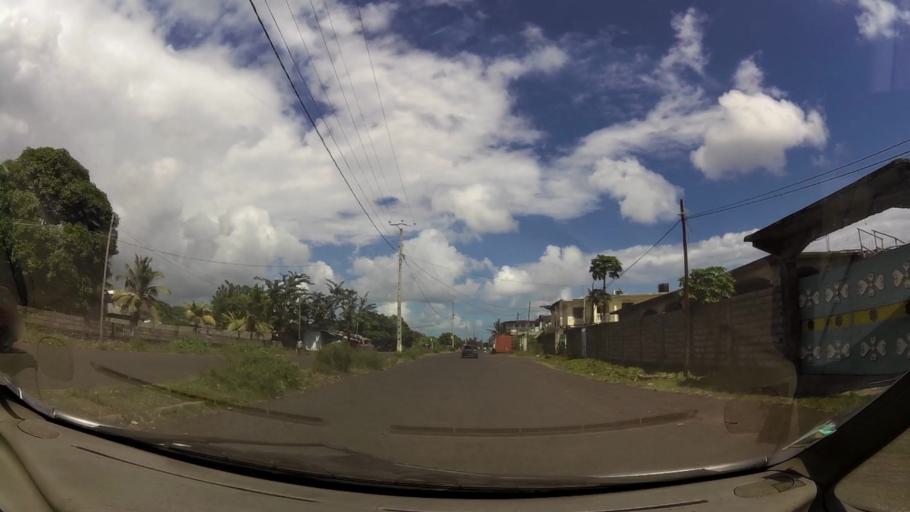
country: KM
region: Grande Comore
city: Mavingouni
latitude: -11.7266
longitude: 43.2443
